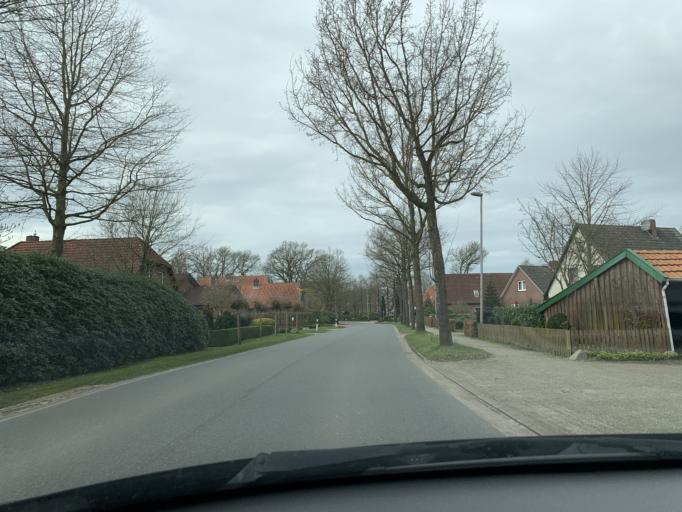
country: DE
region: Lower Saxony
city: Bad Zwischenahn
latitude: 53.1585
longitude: 7.9820
